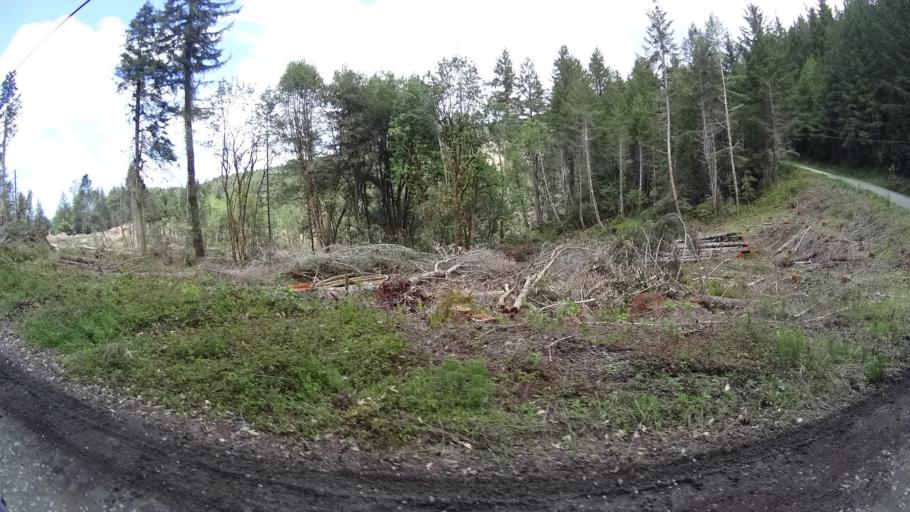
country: US
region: California
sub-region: Humboldt County
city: Blue Lake
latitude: 40.7906
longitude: -123.8793
